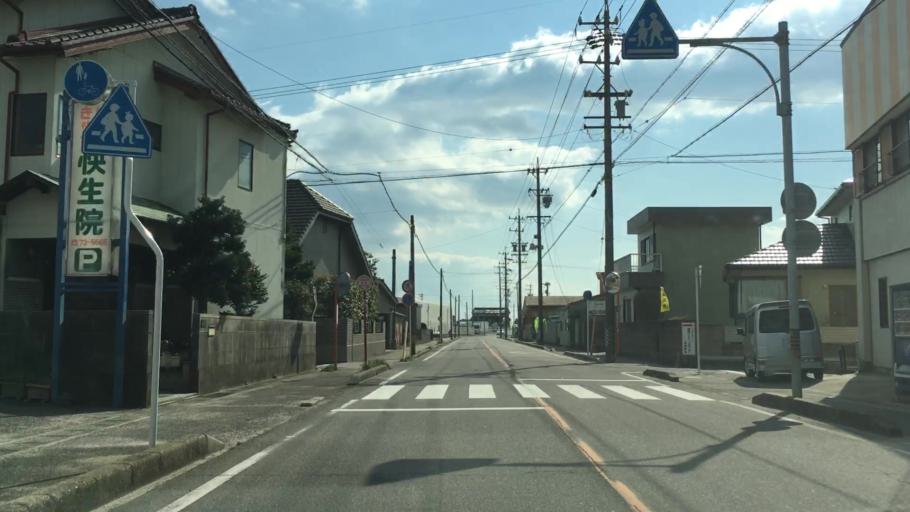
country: JP
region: Aichi
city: Ishiki
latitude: 34.7872
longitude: 137.0321
